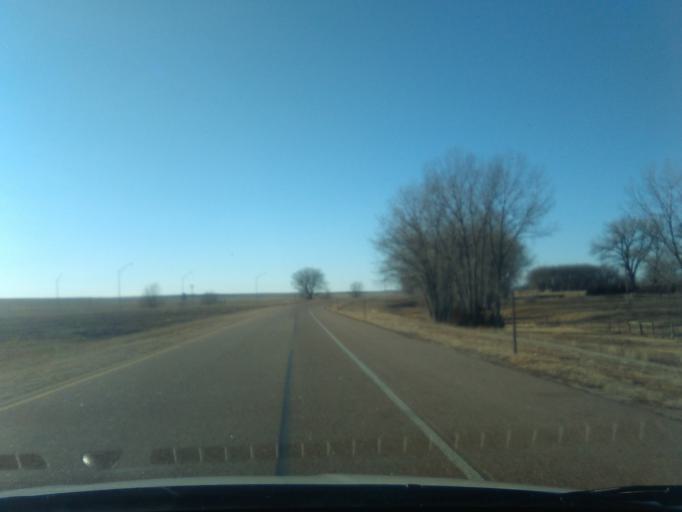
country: US
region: Nebraska
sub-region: Deuel County
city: Chappell
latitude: 41.0823
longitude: -102.4759
